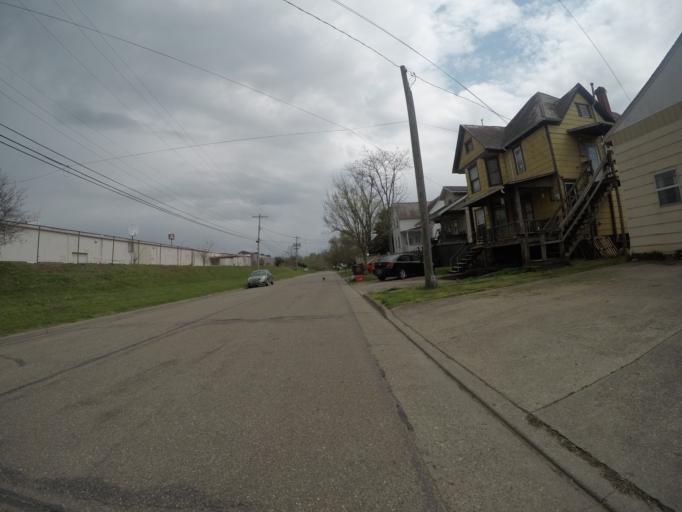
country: US
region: West Virginia
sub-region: Wood County
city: Williamstown
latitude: 39.4087
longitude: -81.4312
